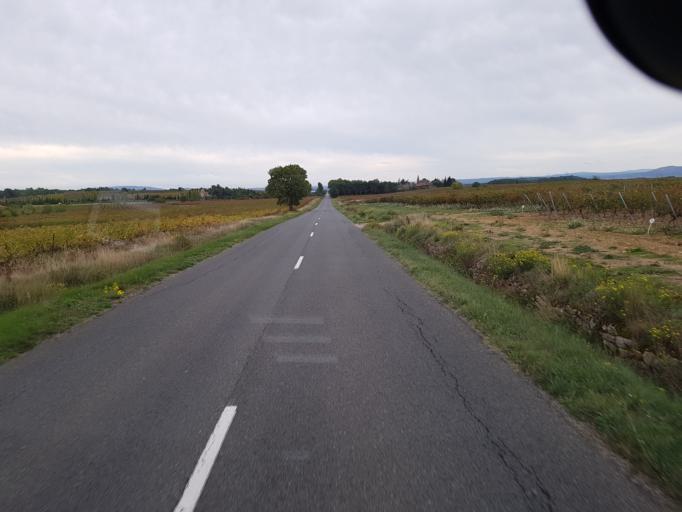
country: FR
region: Languedoc-Roussillon
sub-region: Departement de l'Aude
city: Caunes-Minervois
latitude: 43.3097
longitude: 2.5117
